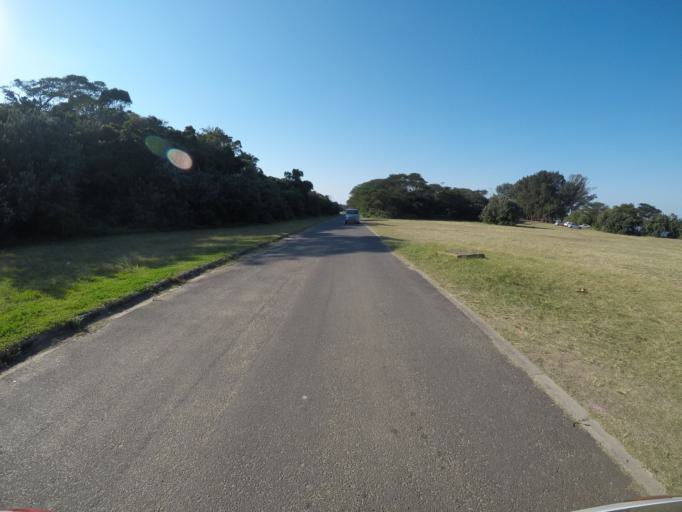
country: ZA
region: KwaZulu-Natal
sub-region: uThungulu District Municipality
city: Richards Bay
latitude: -28.8013
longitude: 32.0803
